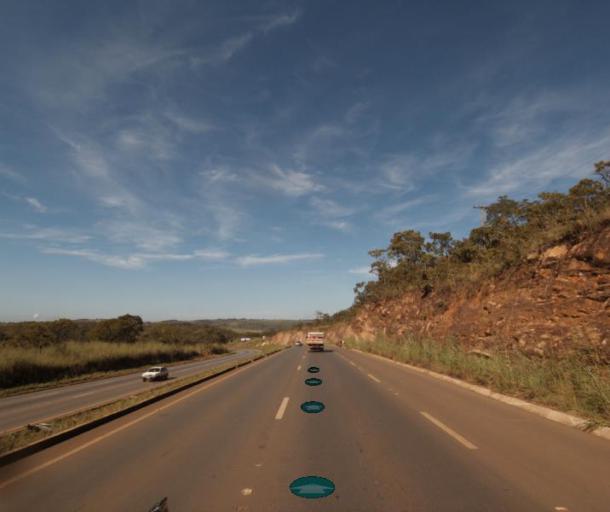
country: BR
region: Federal District
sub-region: Brasilia
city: Brasilia
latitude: -15.7778
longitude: -48.2337
